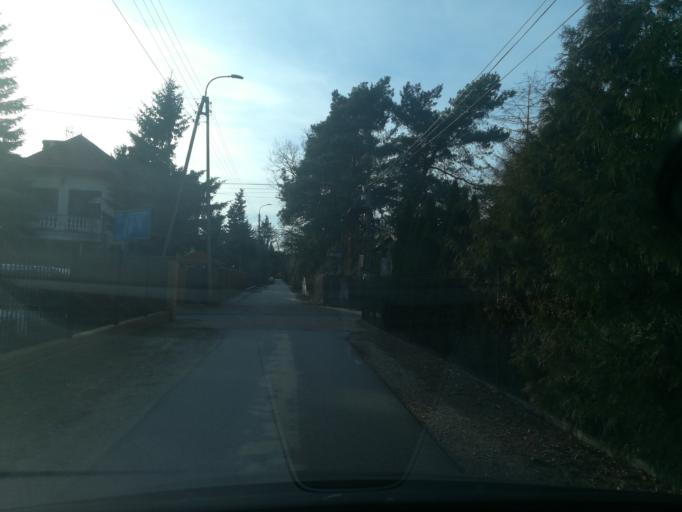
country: PL
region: Masovian Voivodeship
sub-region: Powiat piaseczynski
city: Konstancin-Jeziorna
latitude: 52.0710
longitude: 21.1052
